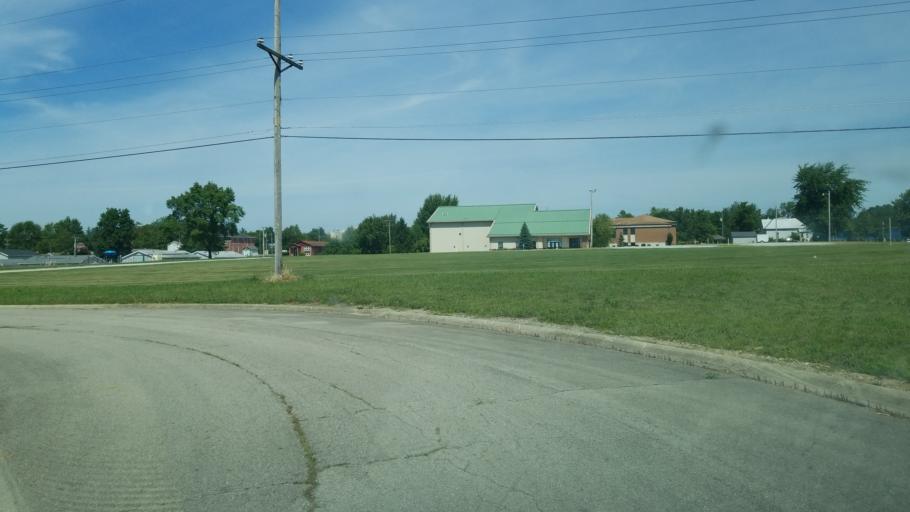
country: US
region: Ohio
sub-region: Hardin County
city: Kenton
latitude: 40.6430
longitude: -83.5945
